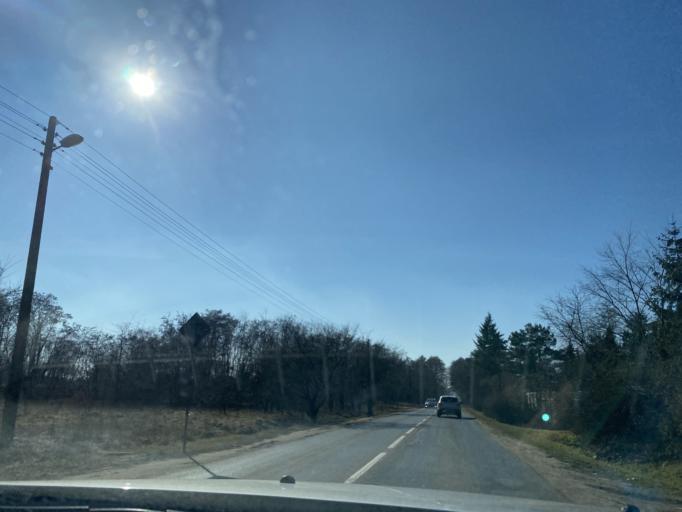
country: PL
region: Greater Poland Voivodeship
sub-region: Powiat poznanski
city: Plewiska
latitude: 52.4064
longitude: 16.8181
